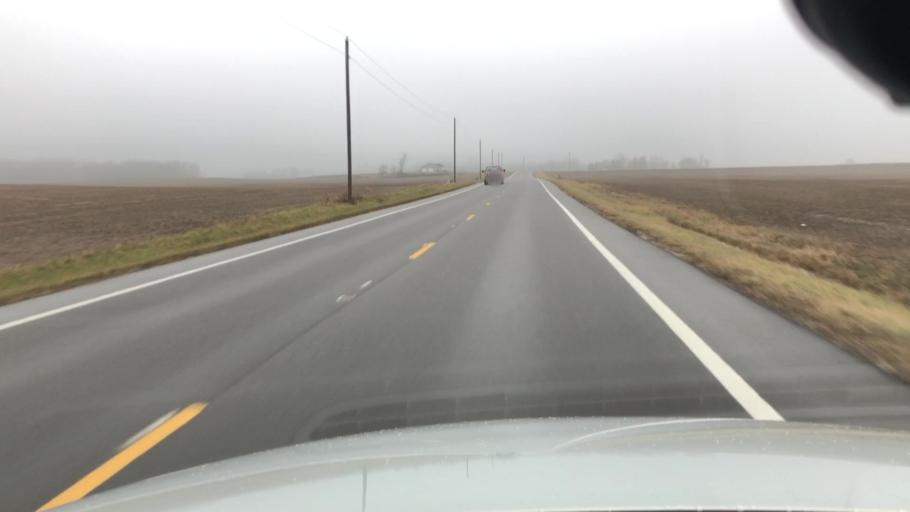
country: US
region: Ohio
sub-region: Logan County
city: Lakeview
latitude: 40.6379
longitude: -83.9231
